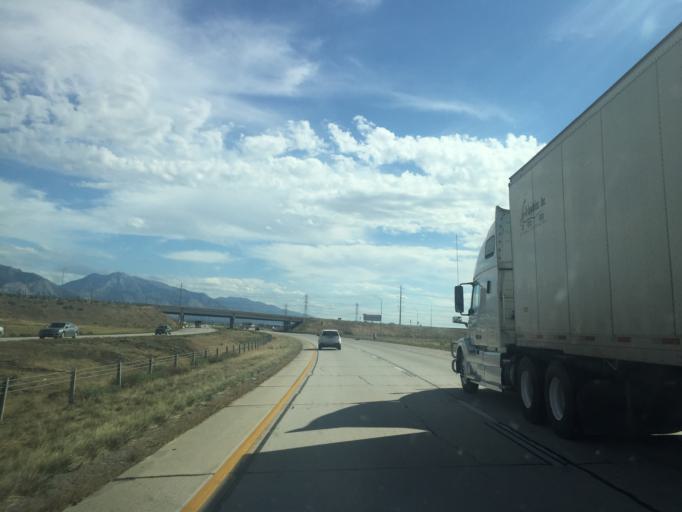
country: US
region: Utah
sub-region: Box Elder County
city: South Willard
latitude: 41.3433
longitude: -112.0387
